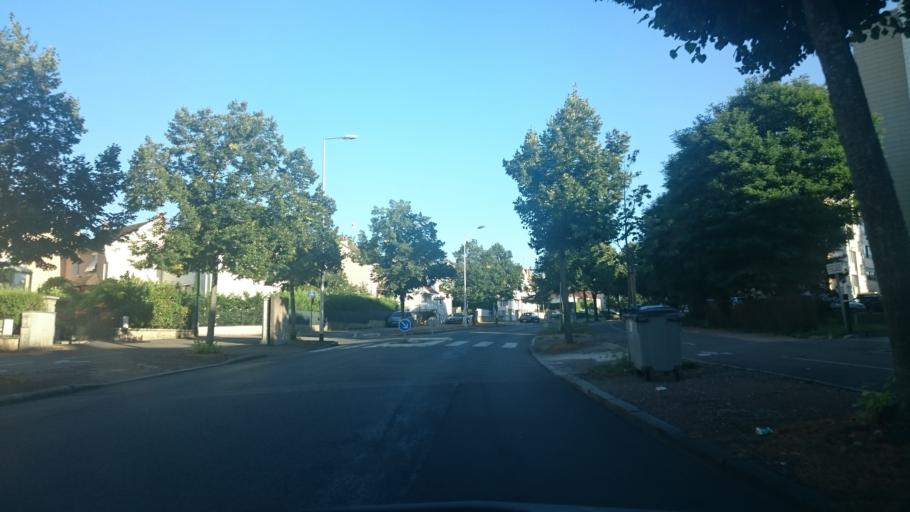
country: FR
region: Bourgogne
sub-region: Departement de la Cote-d'Or
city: Saint-Apollinaire
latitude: 47.3341
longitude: 5.0624
